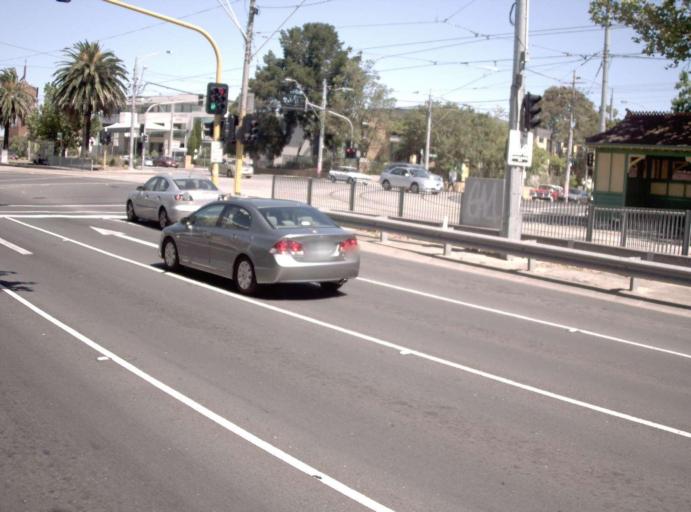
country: AU
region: Victoria
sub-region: Glen Eira
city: Caulfield North
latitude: -37.8652
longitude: 145.0258
